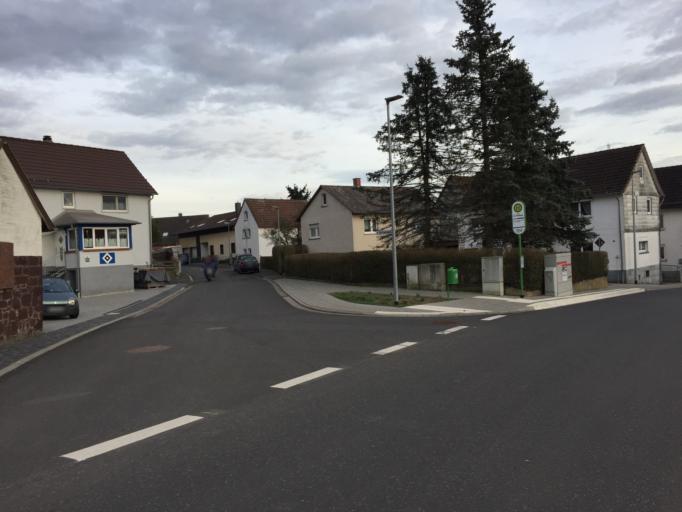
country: DE
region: Hesse
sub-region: Regierungsbezirk Giessen
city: Rabenau
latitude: 50.6901
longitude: 8.8443
